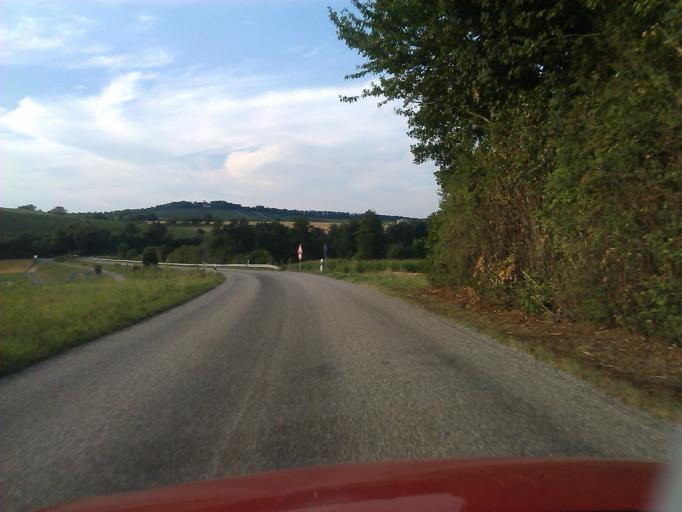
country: DE
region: Baden-Wuerttemberg
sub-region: Regierungsbezirk Stuttgart
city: Pfaffenhofen
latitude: 49.0902
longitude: 8.9618
